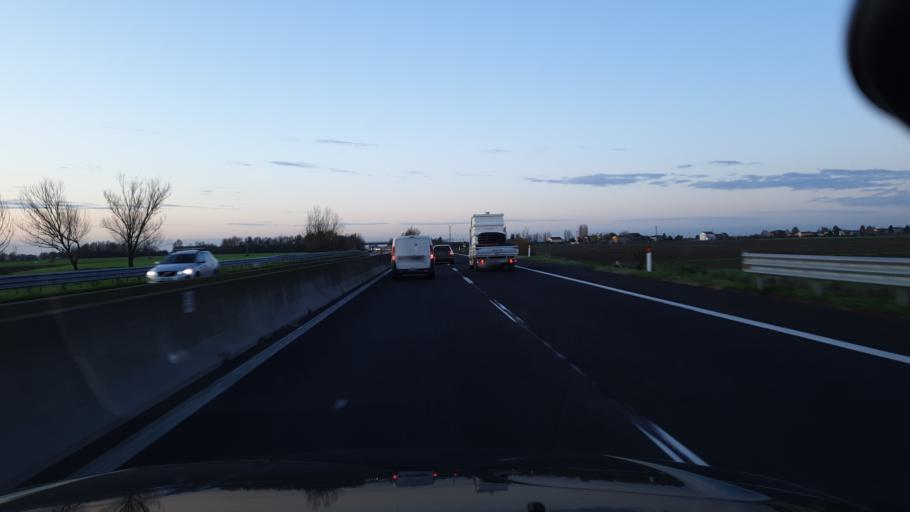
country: IT
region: Veneto
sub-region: Provincia di Rovigo
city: Pincara
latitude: 44.9675
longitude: 11.6484
